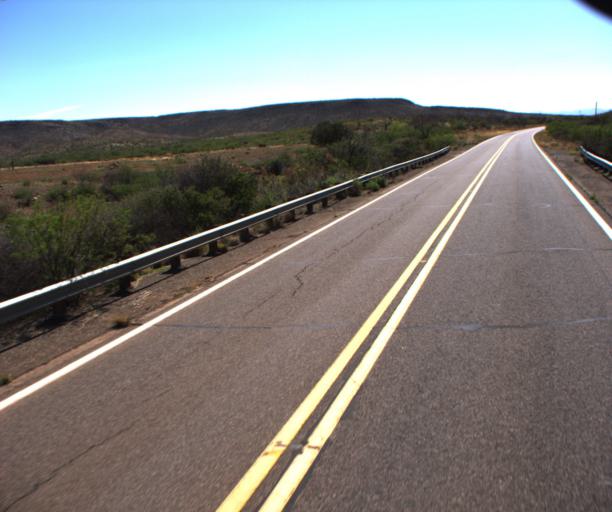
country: US
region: Arizona
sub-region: Cochise County
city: Douglas
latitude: 31.4775
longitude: -109.3989
